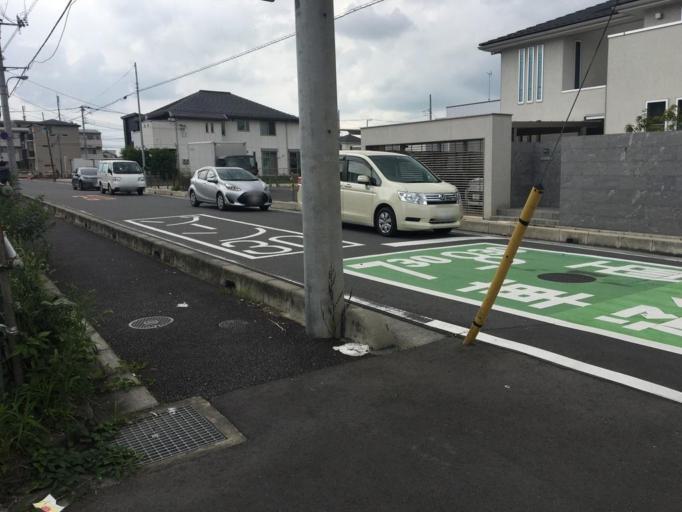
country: JP
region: Saitama
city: Shimotoda
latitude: 35.8185
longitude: 139.6615
